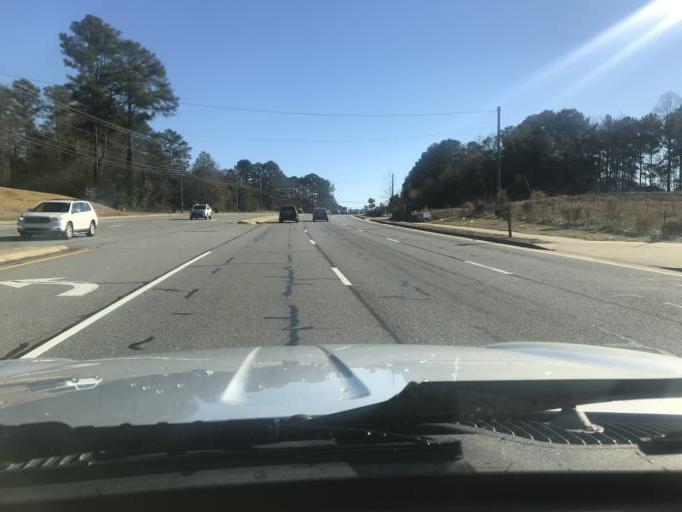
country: US
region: Georgia
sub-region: Gwinnett County
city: Suwanee
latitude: 33.9759
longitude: -84.0715
